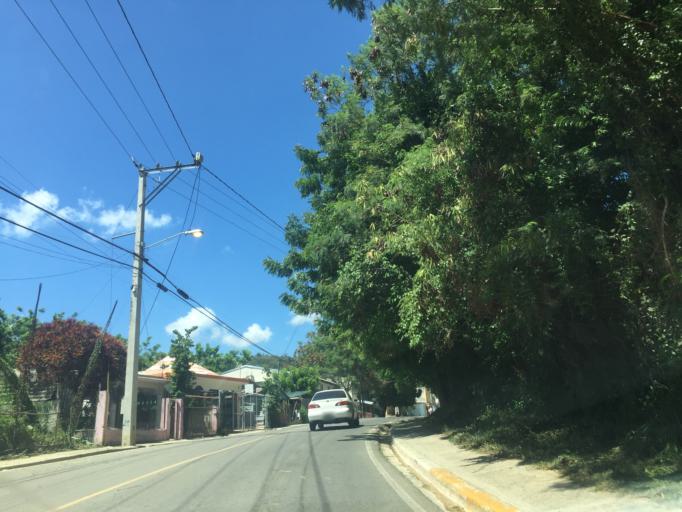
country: DO
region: Santiago
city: Santiago de los Caballeros
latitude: 19.4443
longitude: -70.7427
